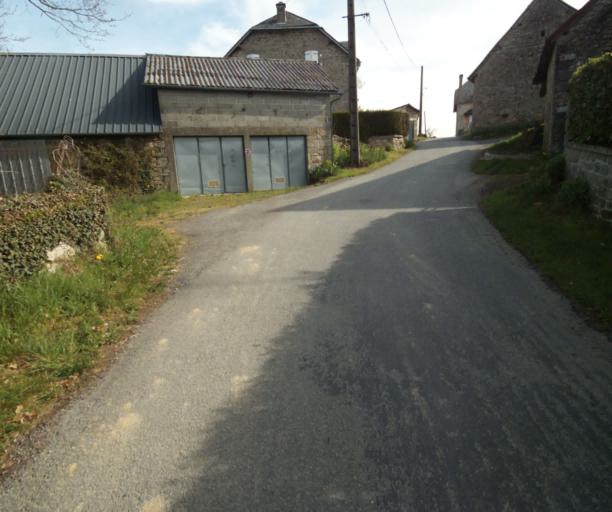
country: FR
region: Limousin
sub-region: Departement de la Correze
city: Correze
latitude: 45.3404
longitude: 1.8372
